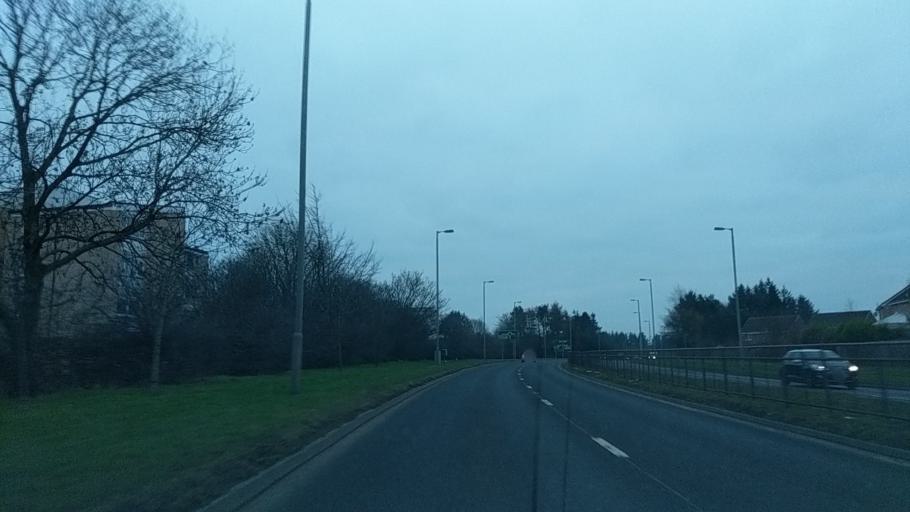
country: GB
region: Scotland
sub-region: South Lanarkshire
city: East Kilbride
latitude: 55.7613
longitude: -4.1647
